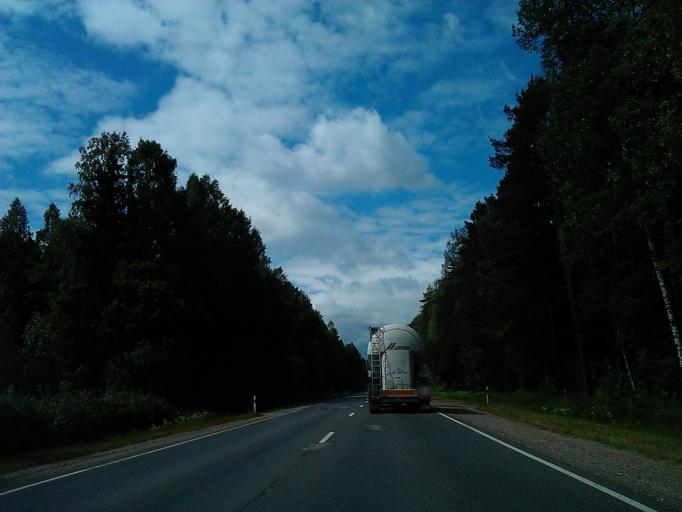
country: LV
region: Engure
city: Smarde
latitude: 56.9182
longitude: 23.3855
